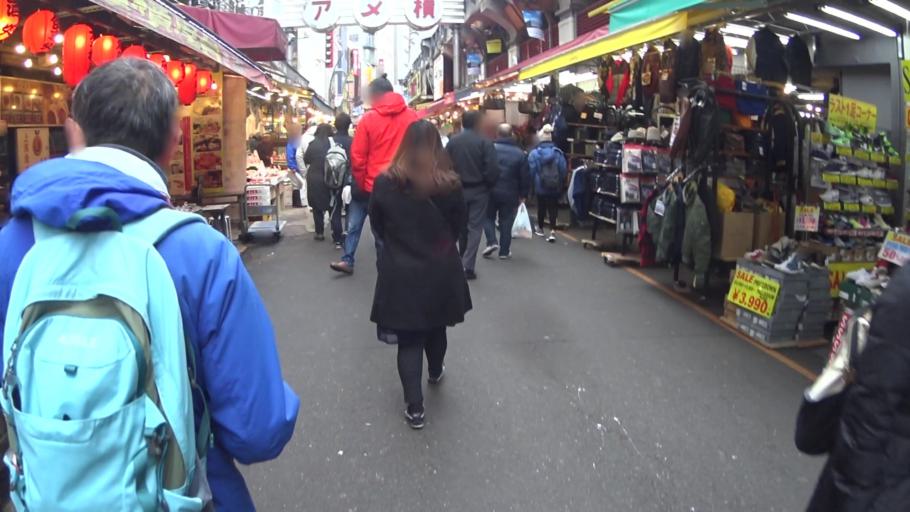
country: JP
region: Tokyo
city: Tokyo
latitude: 35.7101
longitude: 139.7745
